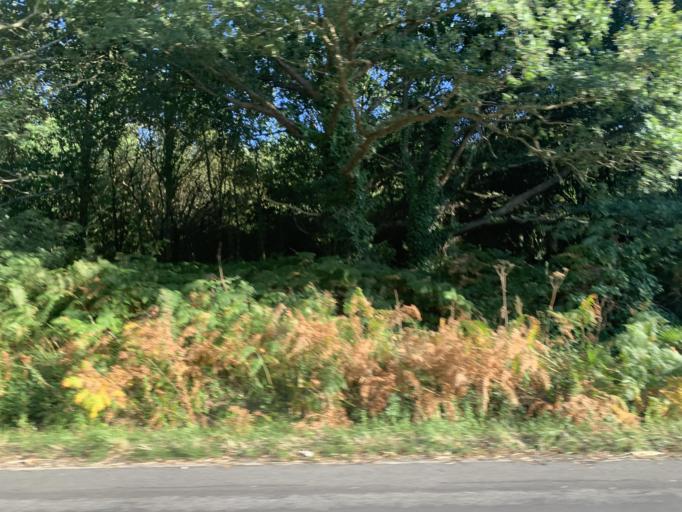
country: FR
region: Pays de la Loire
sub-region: Departement de la Loire-Atlantique
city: Pornichet
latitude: 47.2590
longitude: -2.2970
